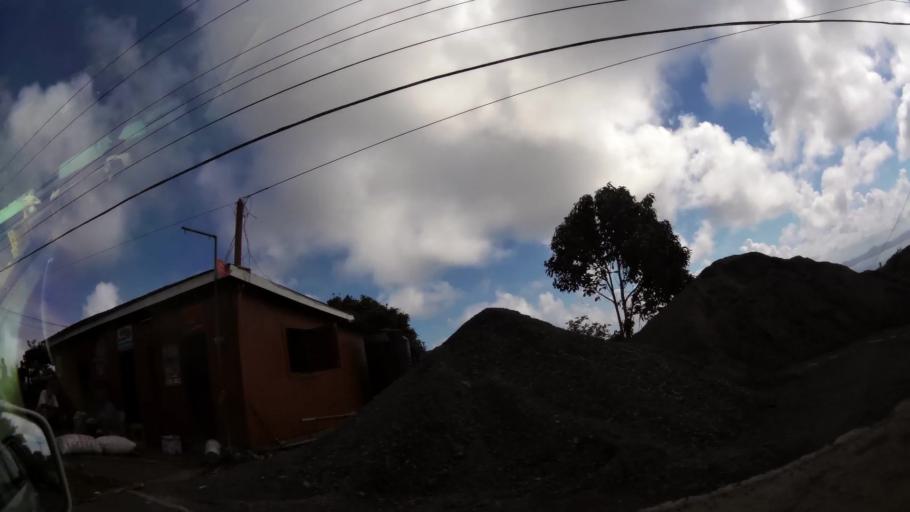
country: VC
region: Saint George
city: Kingstown
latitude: 13.1651
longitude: -61.1801
